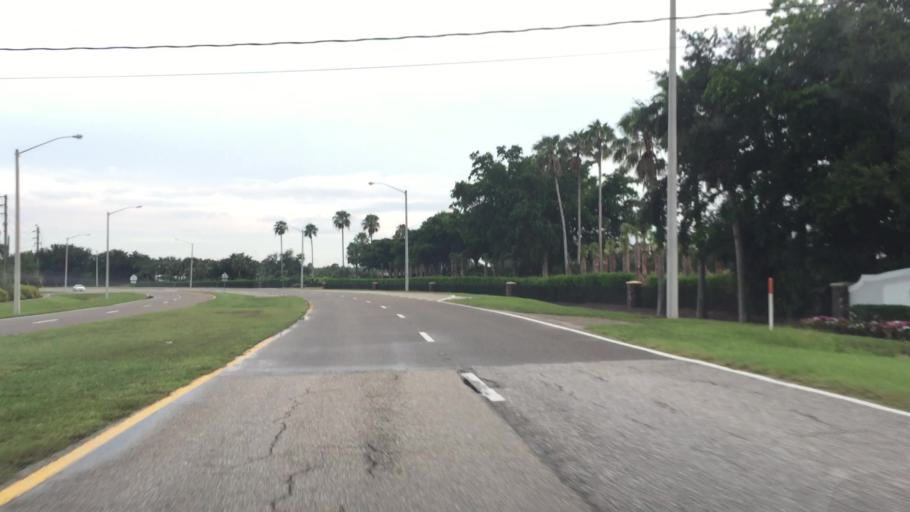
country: US
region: Florida
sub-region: Lee County
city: Fort Myers
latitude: 26.5980
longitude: -81.8176
